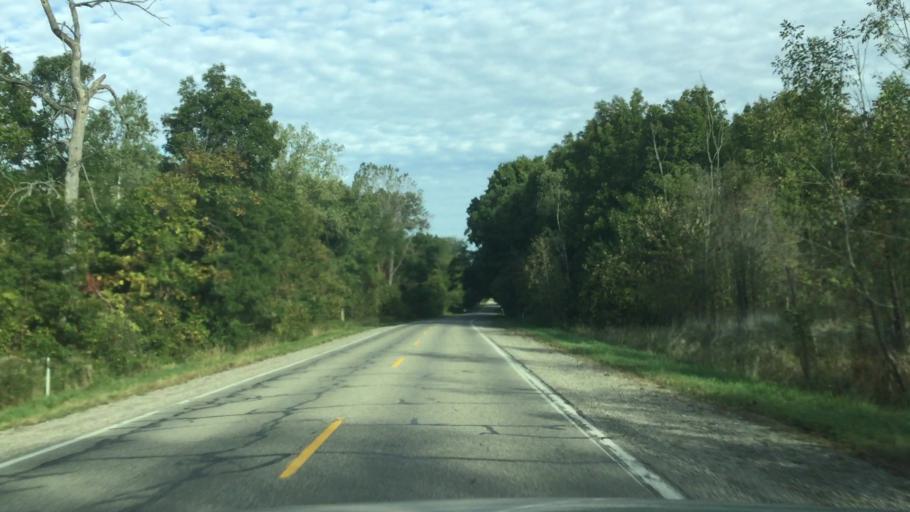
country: US
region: Michigan
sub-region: Livingston County
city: Howell
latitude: 42.5474
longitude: -83.8795
